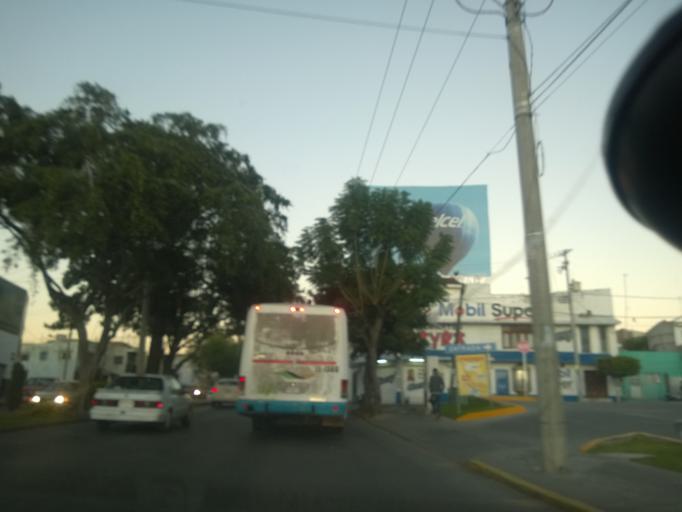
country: MX
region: Guanajuato
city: Leon
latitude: 21.1167
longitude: -101.6902
